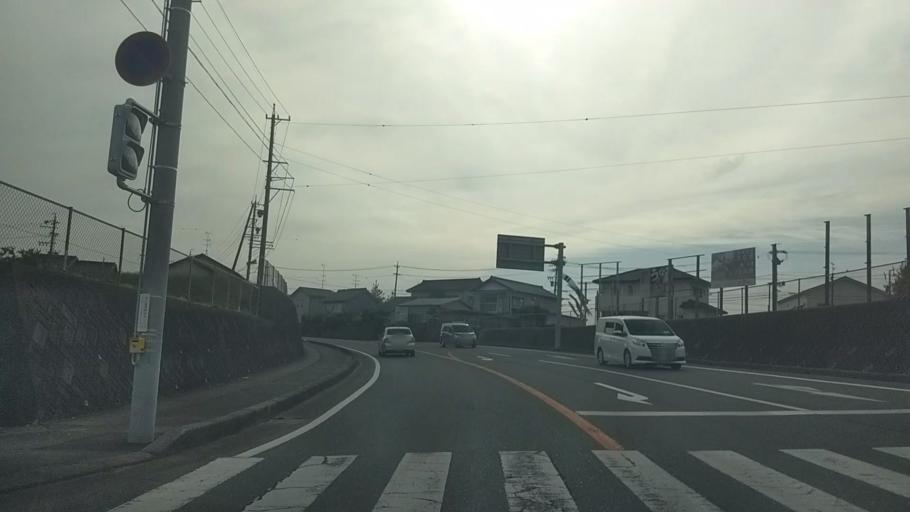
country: JP
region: Shizuoka
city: Hamamatsu
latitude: 34.7649
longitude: 137.6423
